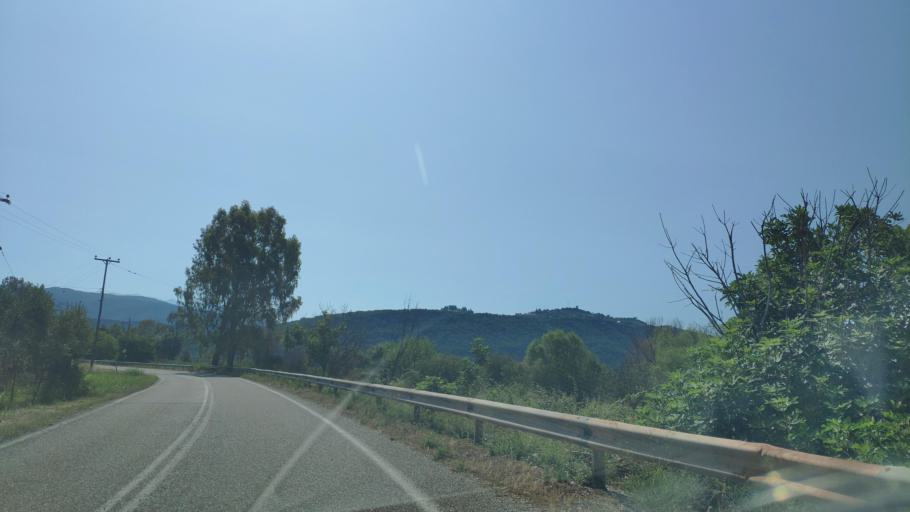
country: GR
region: West Greece
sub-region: Nomos Aitolias kai Akarnanias
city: Lepenou
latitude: 38.7067
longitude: 21.3291
